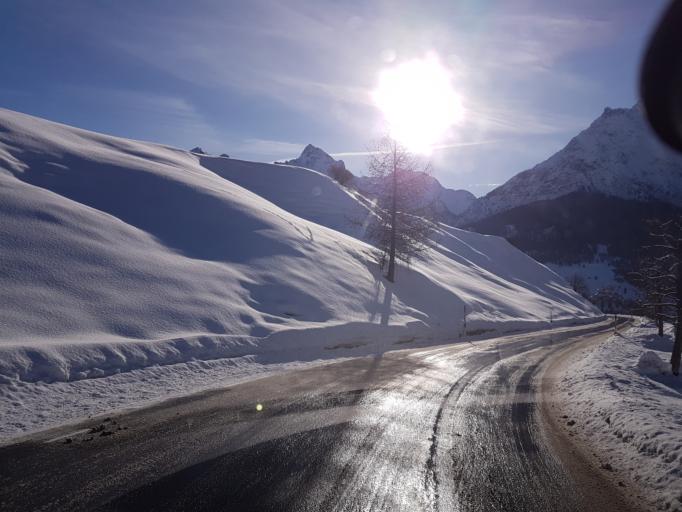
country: CH
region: Grisons
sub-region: Inn District
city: Scuol
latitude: 46.7939
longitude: 10.2500
